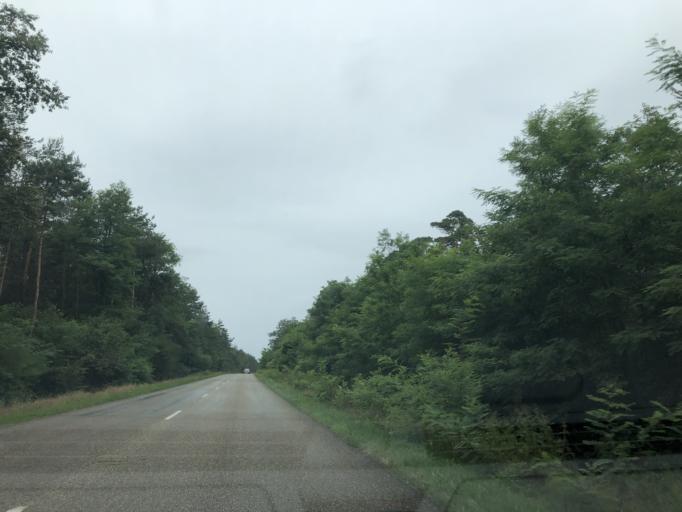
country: DE
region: Rheinland-Pfalz
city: Steinfeld
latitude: 49.0102
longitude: 8.0421
